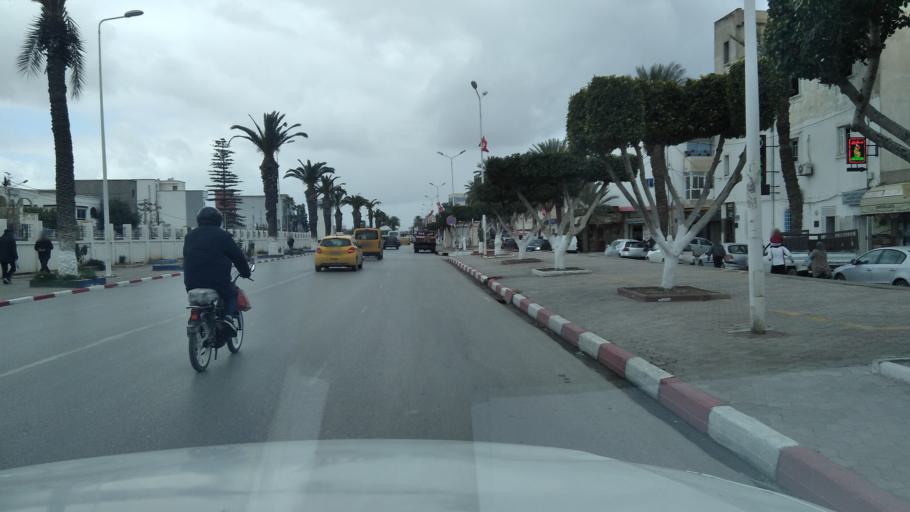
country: TN
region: Bin 'Arus
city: Ben Arous
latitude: 36.7535
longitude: 10.2228
